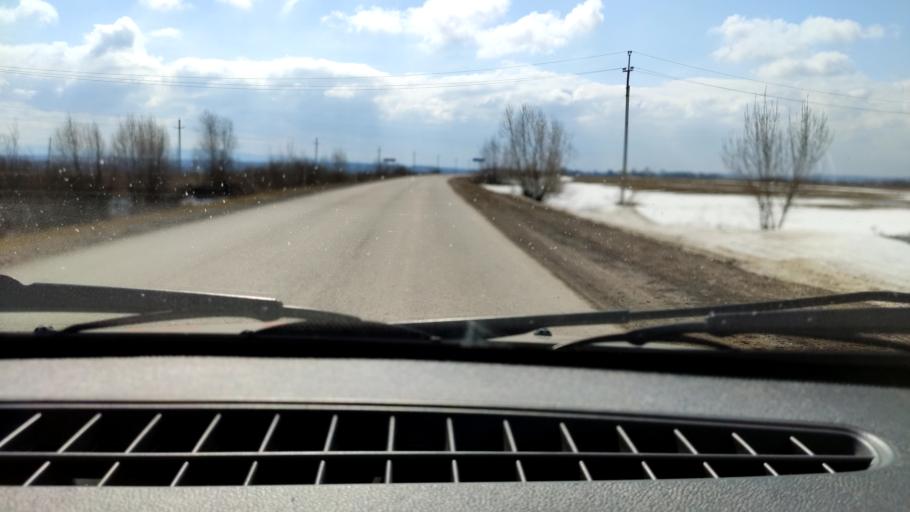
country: RU
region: Bashkortostan
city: Kudeyevskiy
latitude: 54.8445
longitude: 56.7955
